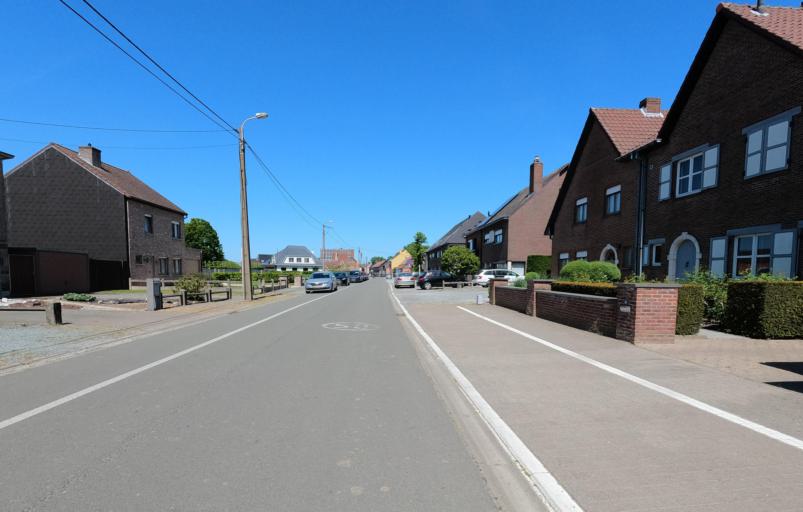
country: BE
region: Flanders
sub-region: Provincie Oost-Vlaanderen
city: Lebbeke
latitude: 50.9947
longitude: 4.1561
